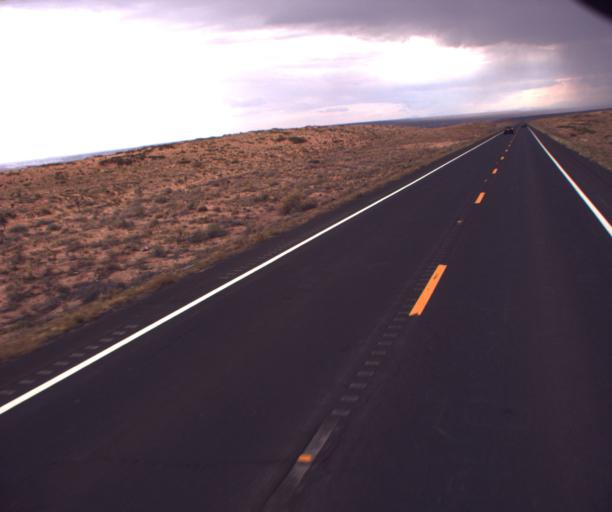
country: US
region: Arizona
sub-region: Coconino County
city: Tuba City
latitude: 36.2291
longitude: -111.0333
